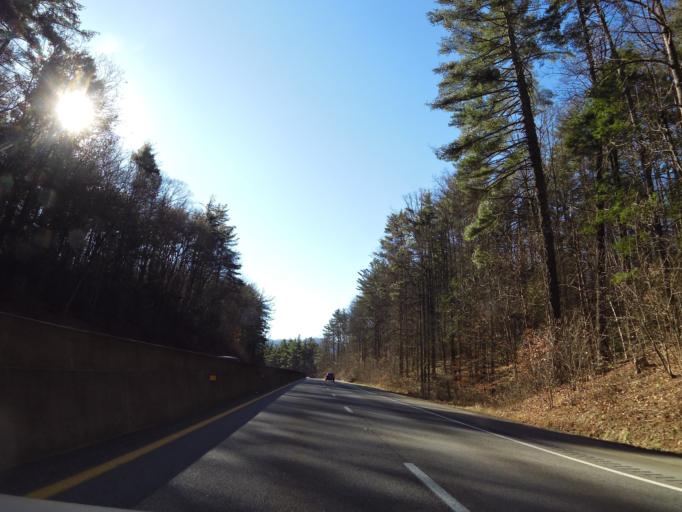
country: US
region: North Carolina
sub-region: Haywood County
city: Cove Creek
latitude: 35.6847
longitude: -83.0297
